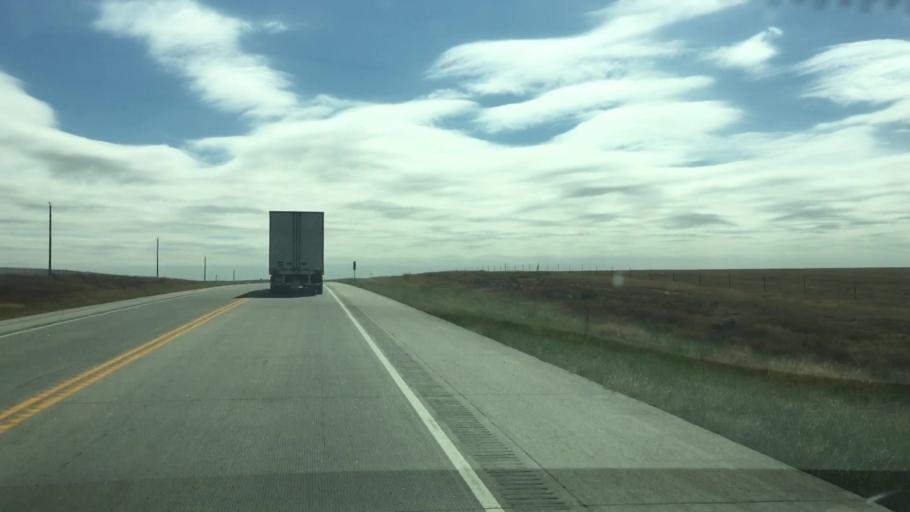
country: US
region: Colorado
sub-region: Lincoln County
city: Hugo
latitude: 39.0085
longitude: -103.2961
